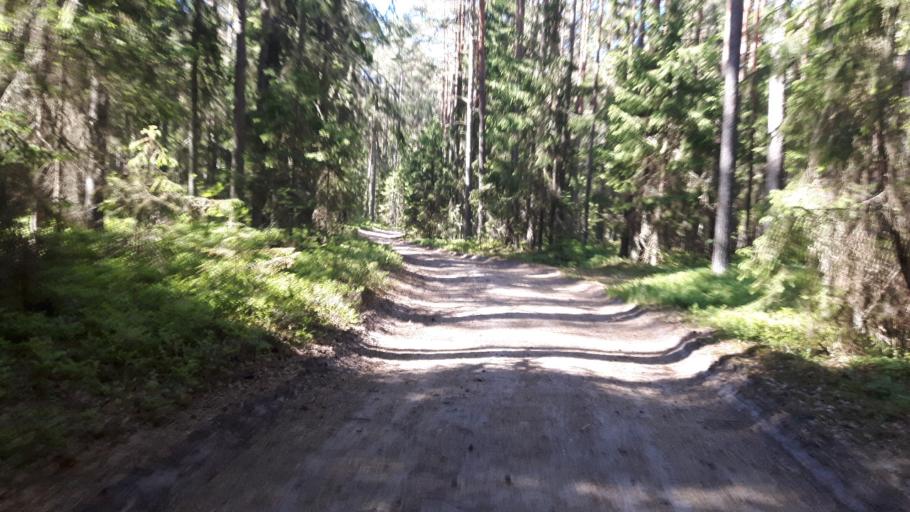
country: EE
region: Harju
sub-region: Loksa linn
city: Loksa
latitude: 59.5634
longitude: 25.8338
